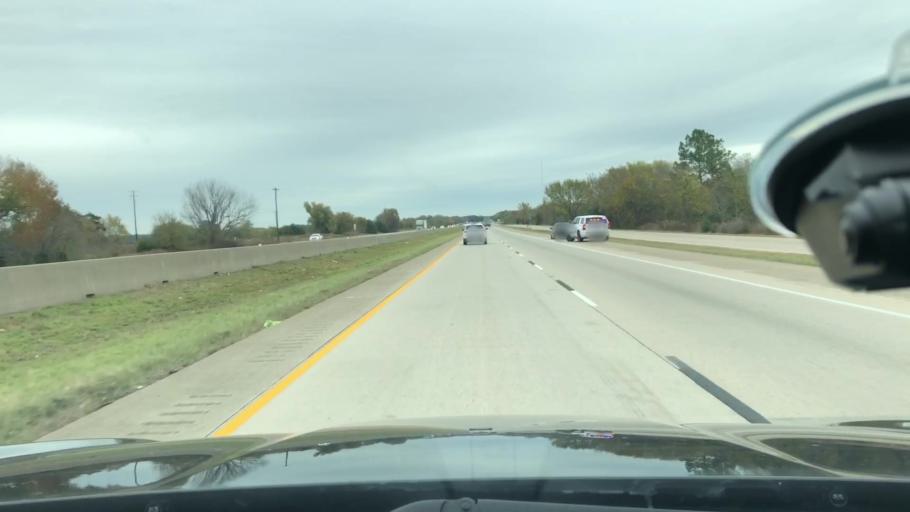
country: US
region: Texas
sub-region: Hopkins County
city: Sulphur Springs
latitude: 33.1286
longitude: -95.7617
